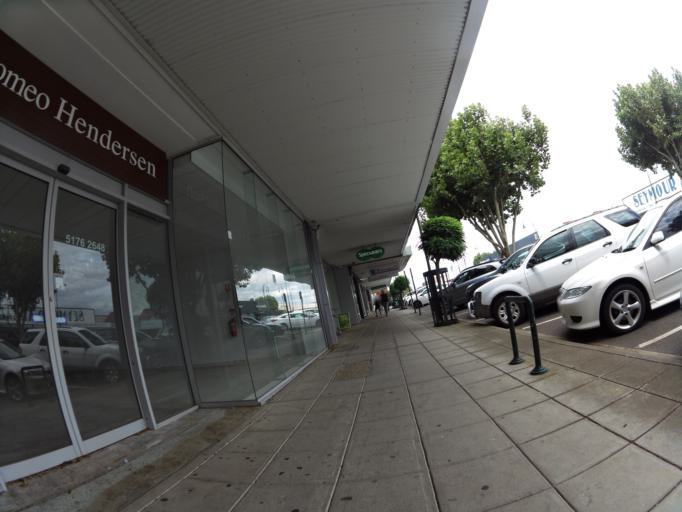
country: AU
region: Victoria
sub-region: Latrobe
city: Traralgon
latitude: -38.1962
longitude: 146.5367
